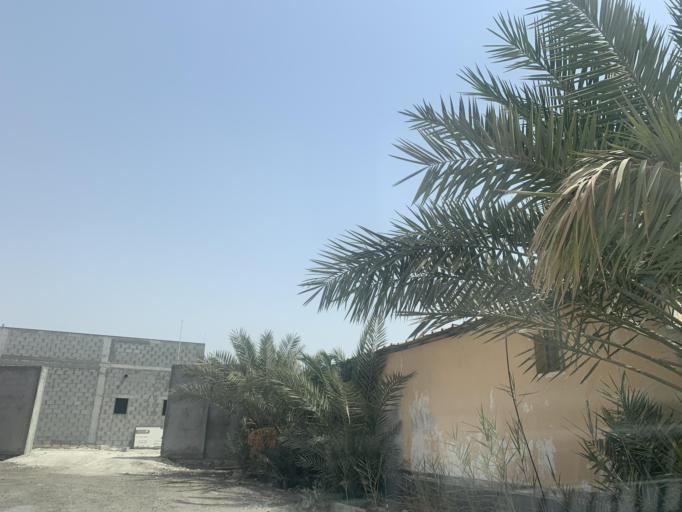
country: BH
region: Northern
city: Madinat `Isa
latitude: 26.1880
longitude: 50.4934
